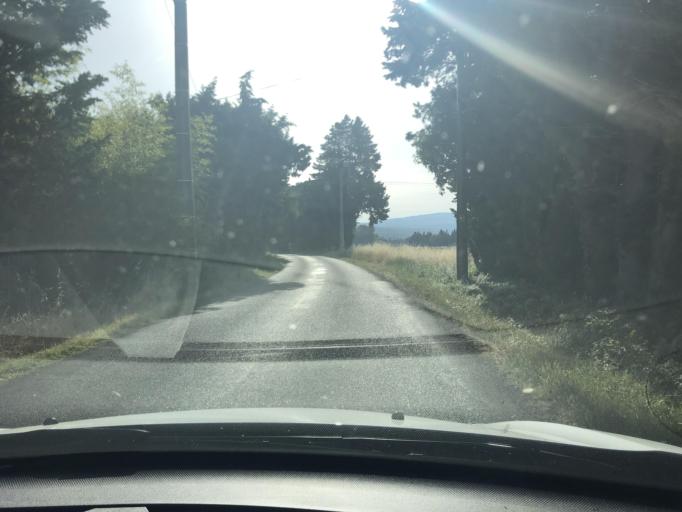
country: FR
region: Provence-Alpes-Cote d'Azur
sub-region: Departement du Vaucluse
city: Velleron
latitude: 43.9651
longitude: 5.0140
